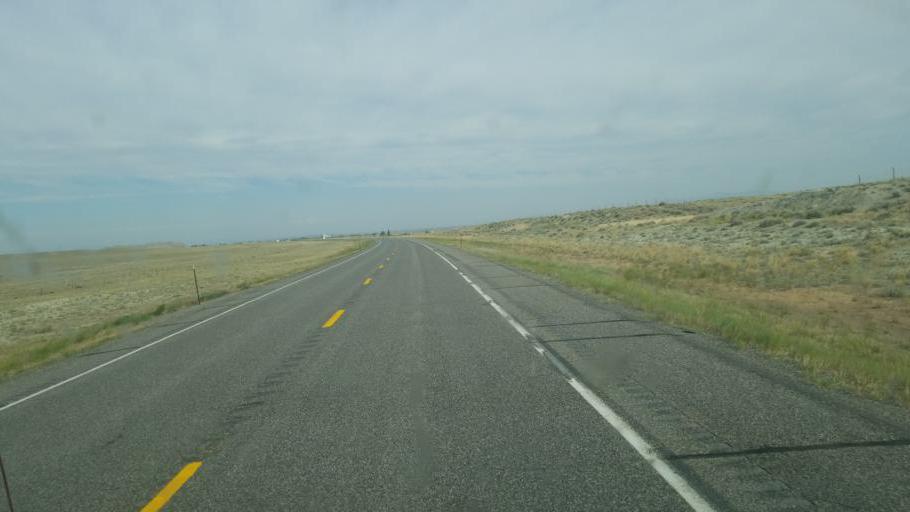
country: US
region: Wyoming
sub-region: Fremont County
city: Riverton
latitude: 43.2358
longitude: -108.0753
